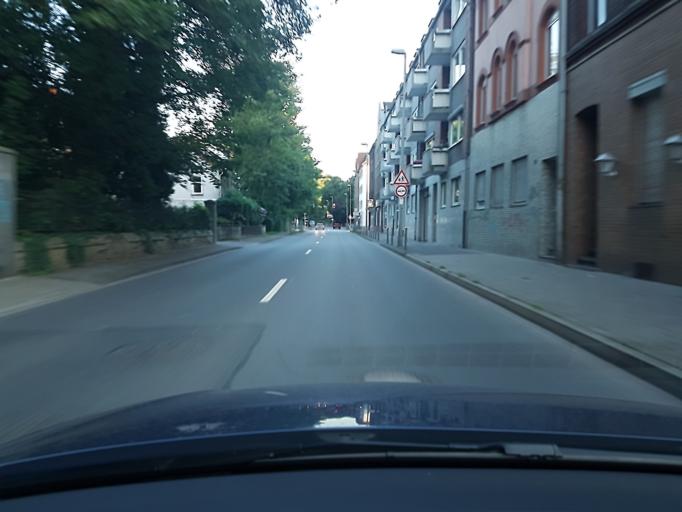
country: DE
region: North Rhine-Westphalia
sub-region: Regierungsbezirk Dusseldorf
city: Erkrath
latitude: 51.2184
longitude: 6.8658
